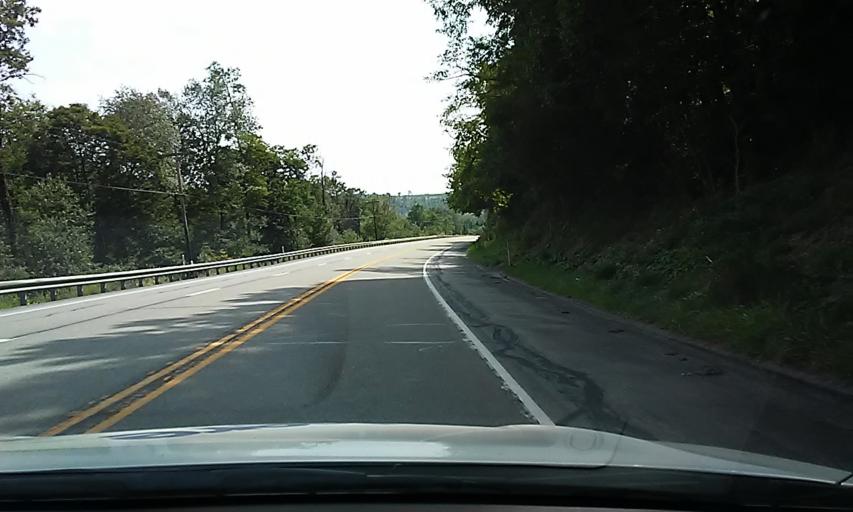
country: US
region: Pennsylvania
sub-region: Jefferson County
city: Punxsutawney
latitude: 40.8287
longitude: -79.0387
